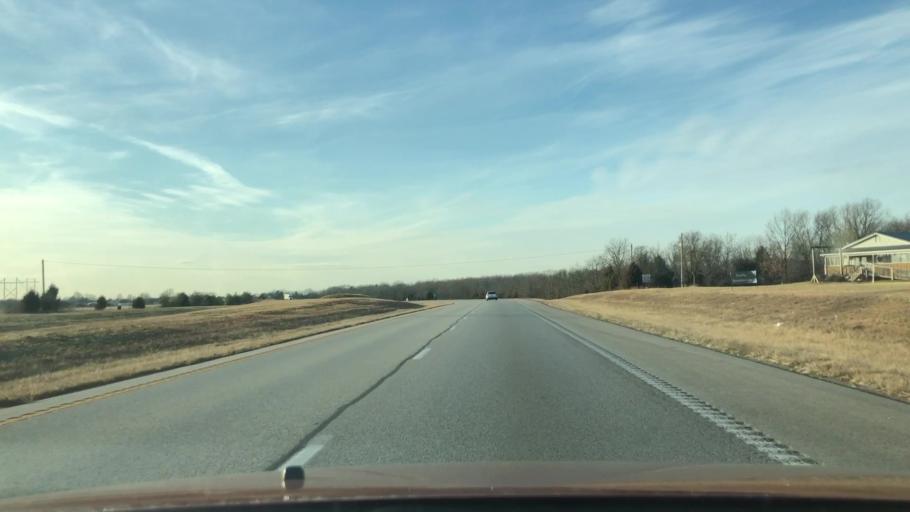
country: US
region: Missouri
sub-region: Webster County
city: Seymour
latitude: 37.1168
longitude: -92.6784
